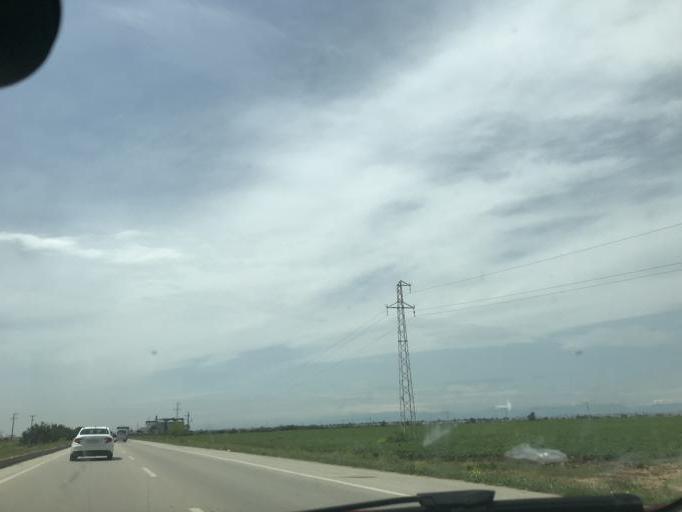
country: TR
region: Adana
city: Yuregir
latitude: 36.9765
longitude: 35.4804
